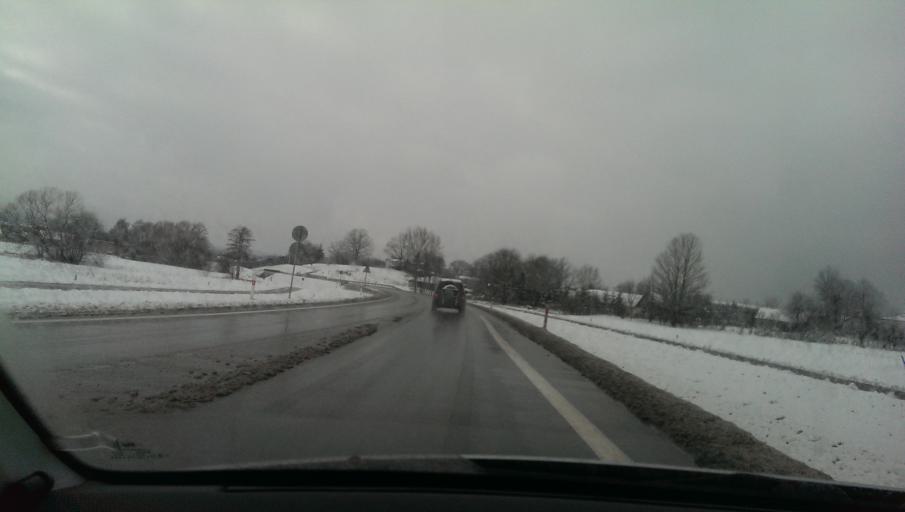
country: PL
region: Subcarpathian Voivodeship
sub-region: Powiat brzozowski
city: Brzozow
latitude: 49.7023
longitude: 22.0341
